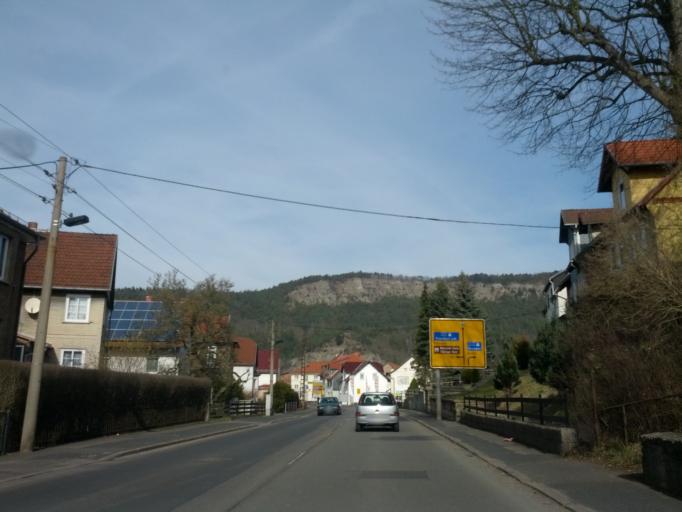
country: DE
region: Thuringia
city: Thal
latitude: 50.9547
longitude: 10.3951
